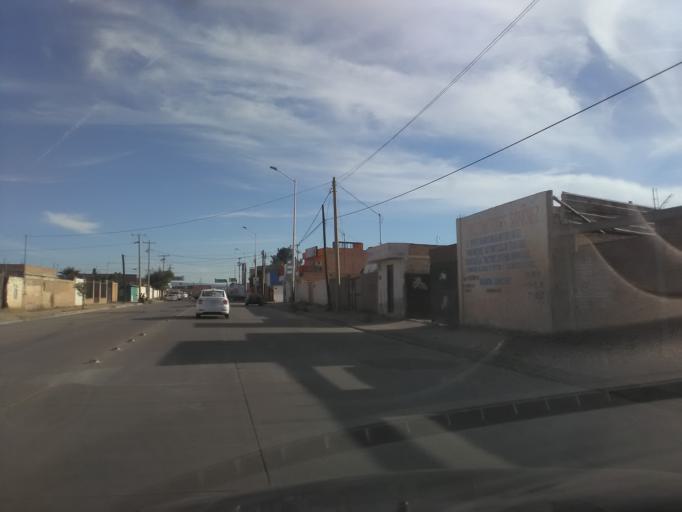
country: MX
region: Durango
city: Victoria de Durango
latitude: 24.0139
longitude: -104.6223
